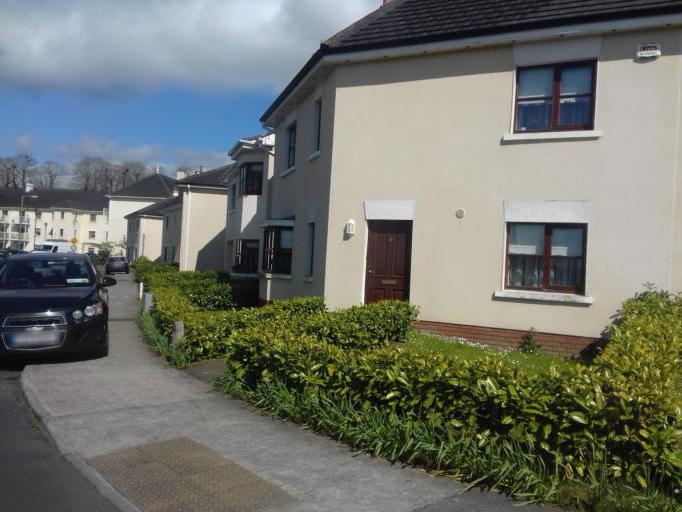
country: IE
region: Leinster
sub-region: Laois
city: Portlaoise
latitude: 53.0419
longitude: -7.2680
